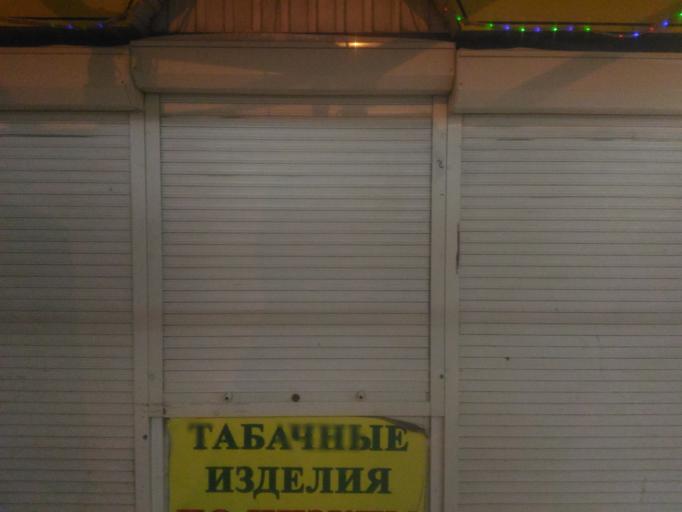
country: RU
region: Ulyanovsk
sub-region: Ulyanovskiy Rayon
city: Ulyanovsk
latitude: 54.3077
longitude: 48.3502
